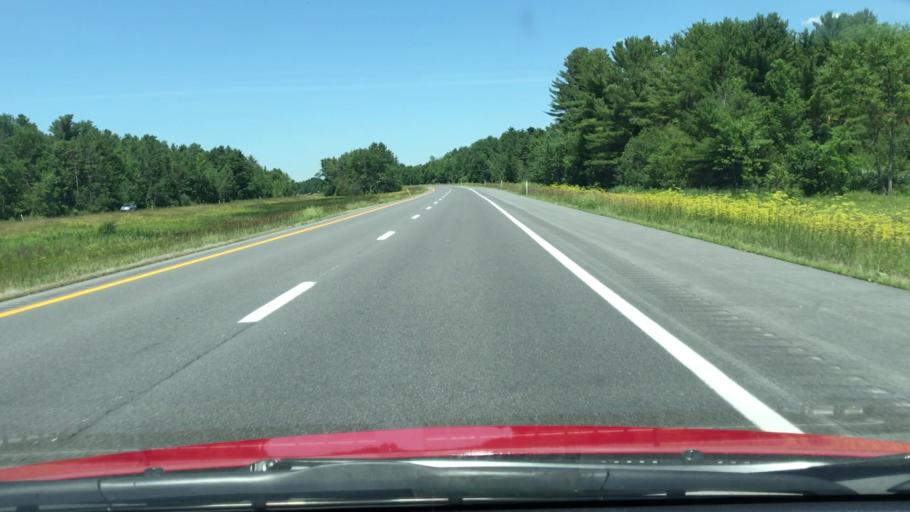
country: US
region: New York
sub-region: Clinton County
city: Cumberland Head
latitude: 44.8396
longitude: -73.4463
